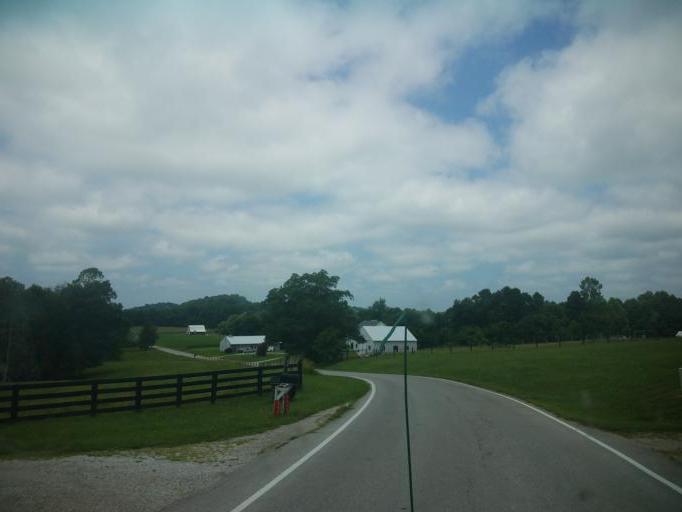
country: US
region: Kentucky
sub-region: Hart County
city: Munfordville
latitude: 37.3378
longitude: -86.0263
